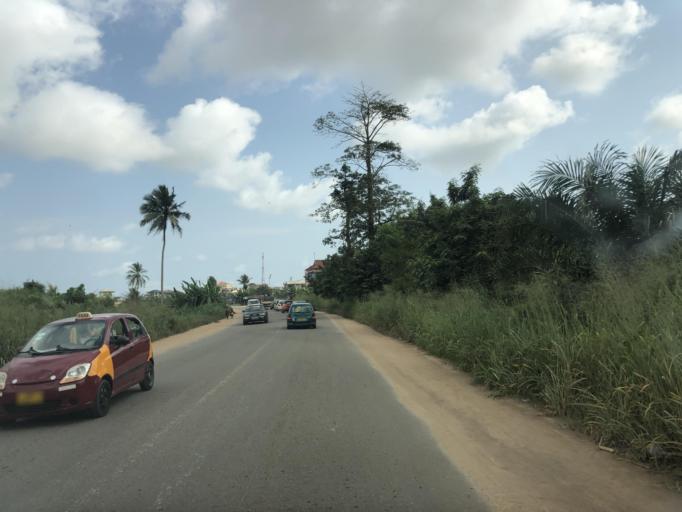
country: GH
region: Central
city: Cape Coast
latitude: 5.1462
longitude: -1.2872
